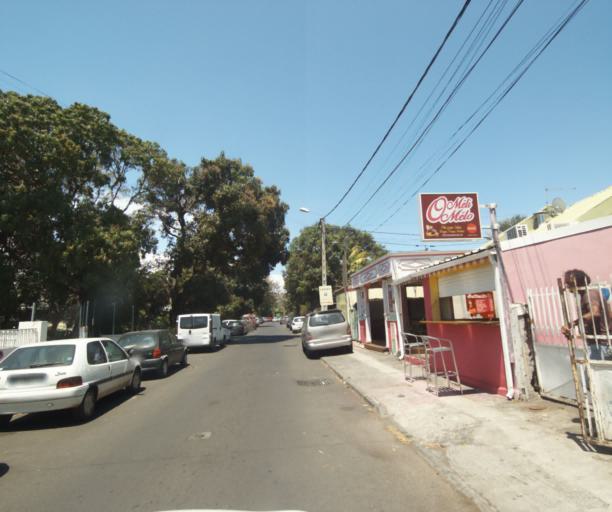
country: RE
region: Reunion
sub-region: Reunion
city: Saint-Paul
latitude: -21.0054
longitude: 55.2750
